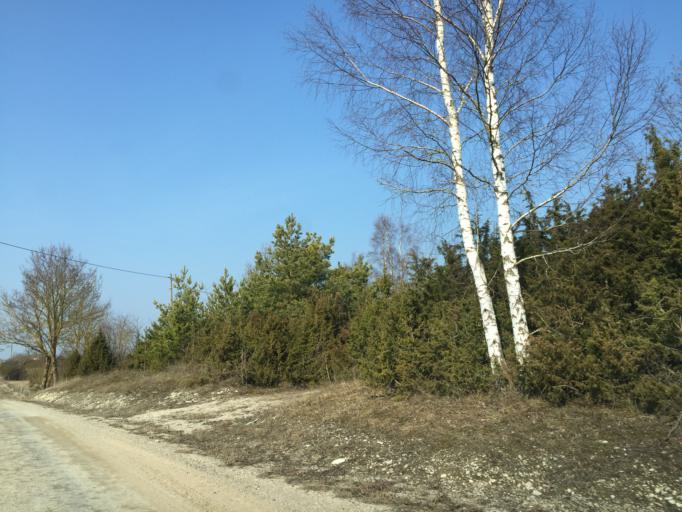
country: EE
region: Saare
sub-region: Orissaare vald
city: Orissaare
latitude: 58.4798
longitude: 23.1236
